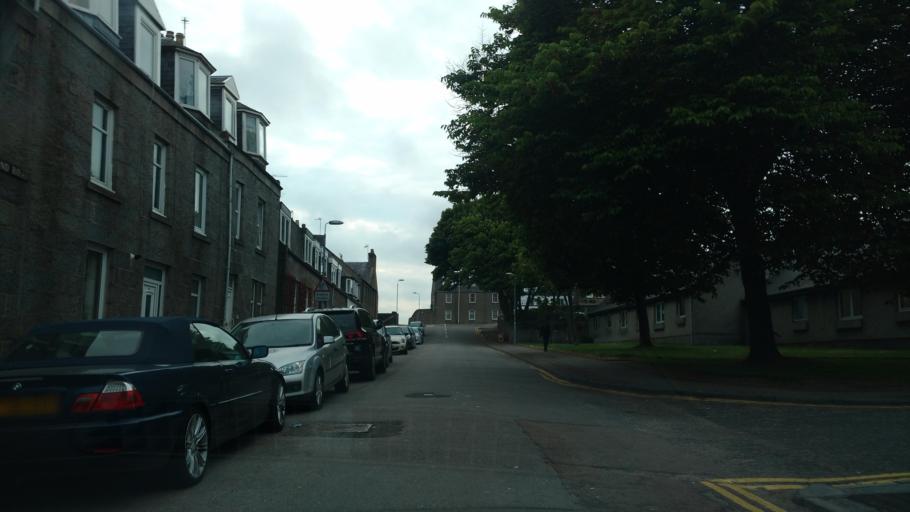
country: GB
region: Scotland
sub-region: Aberdeen City
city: Aberdeen
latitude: 57.1585
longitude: -2.0977
